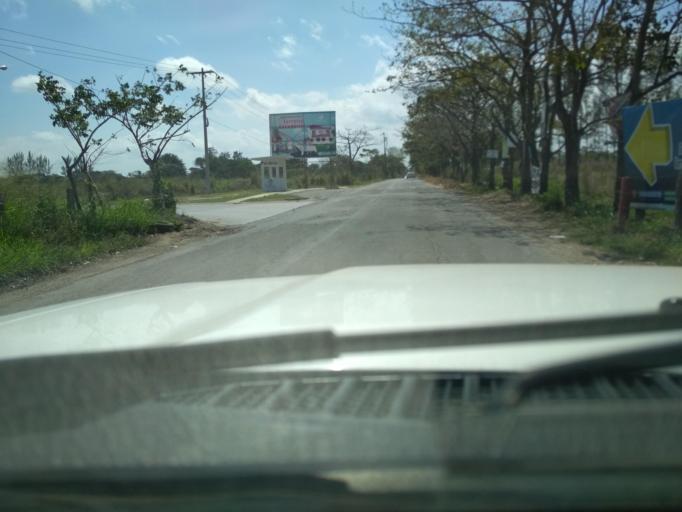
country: MX
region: Veracruz
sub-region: Veracruz
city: Las Amapolas
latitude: 19.1346
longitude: -96.2159
